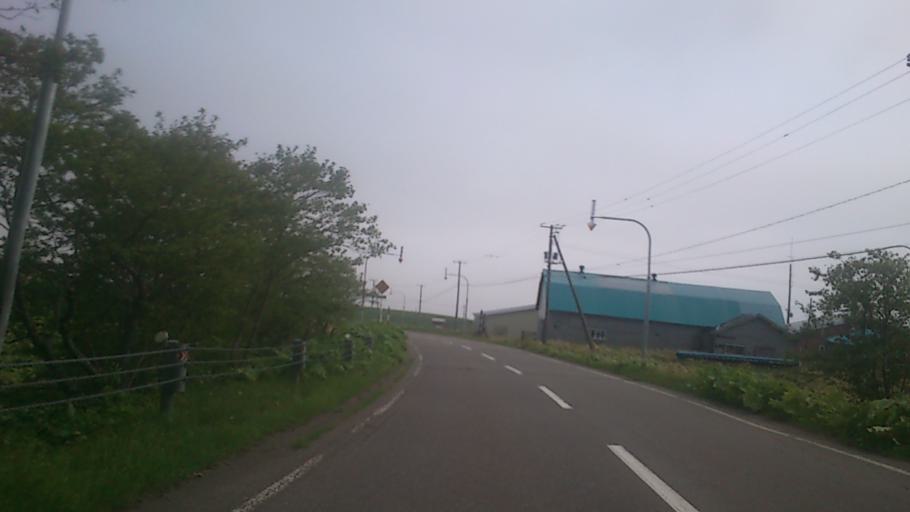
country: JP
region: Hokkaido
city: Nemuro
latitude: 43.1861
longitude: 145.3240
